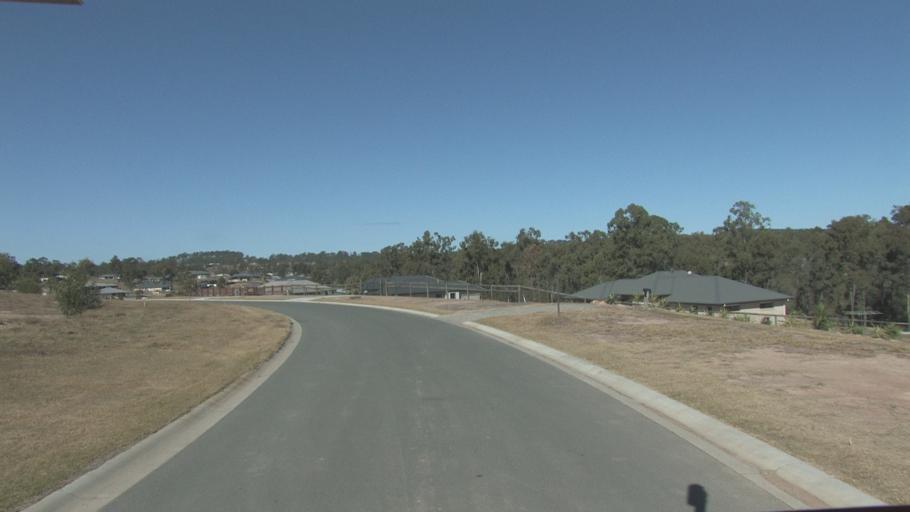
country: AU
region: Queensland
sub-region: Logan
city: Cedar Vale
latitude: -27.8630
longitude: 153.0425
